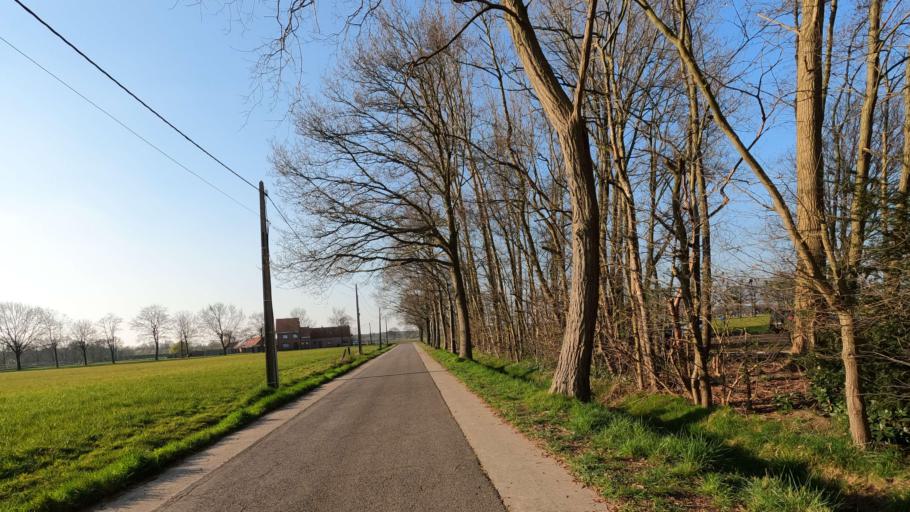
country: BE
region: Flanders
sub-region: Provincie Antwerpen
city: Beerse
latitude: 51.3333
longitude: 4.8295
